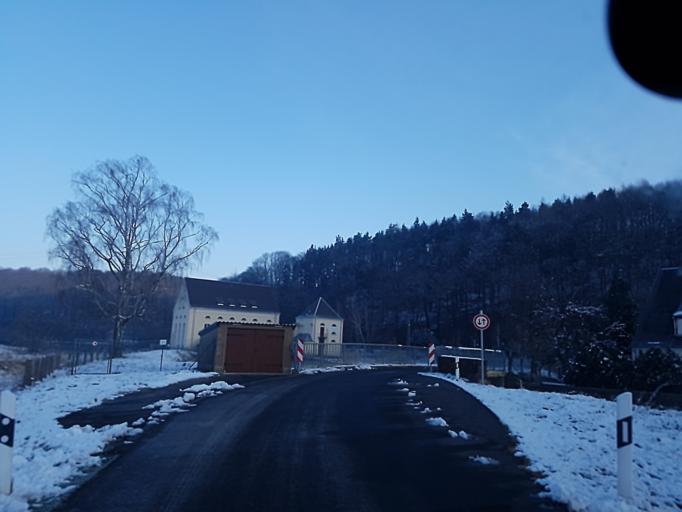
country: DE
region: Saxony
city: Grossweitzschen
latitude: 51.1527
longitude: 13.0101
